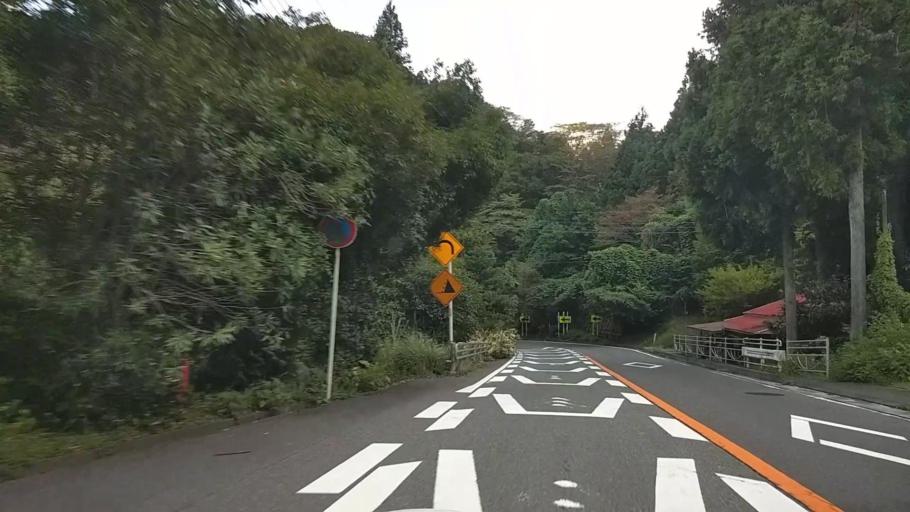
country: JP
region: Shizuoka
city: Fujinomiya
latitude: 35.3213
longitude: 138.4361
